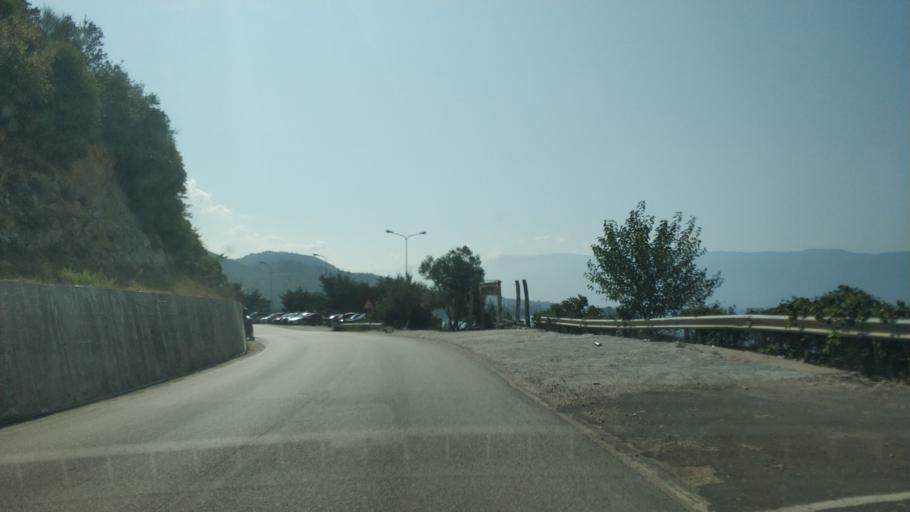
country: AL
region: Vlore
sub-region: Rrethi i Vlores
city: Orikum
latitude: 40.3929
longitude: 19.4795
